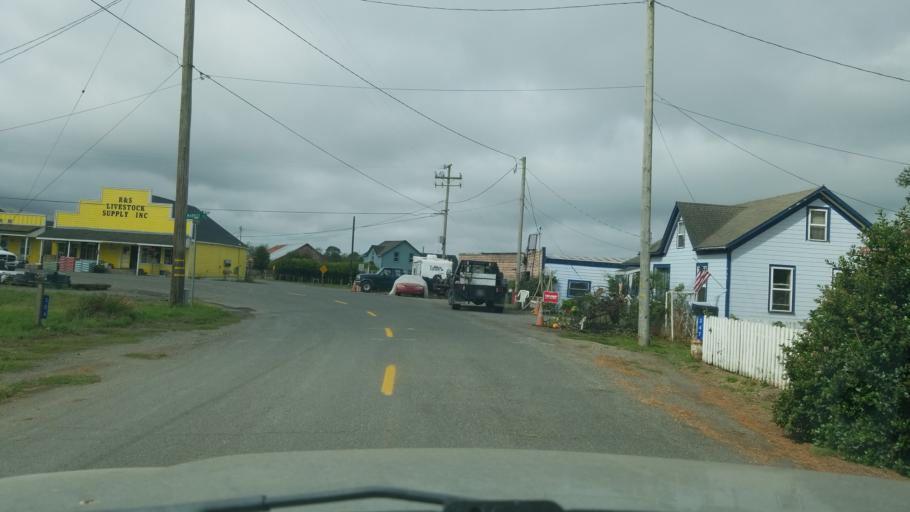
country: US
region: California
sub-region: Humboldt County
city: Ferndale
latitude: 40.5948
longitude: -124.2547
